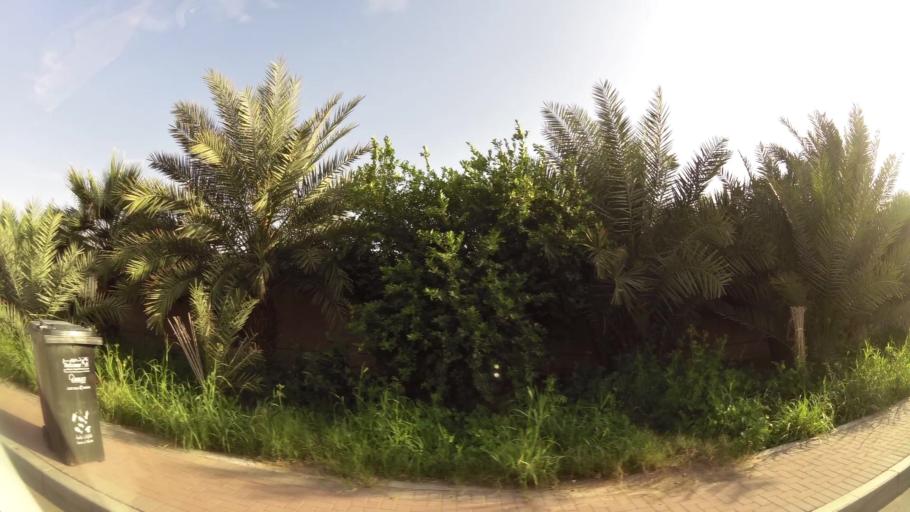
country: AE
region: Abu Dhabi
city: Al Ain
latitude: 24.0795
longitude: 55.8417
